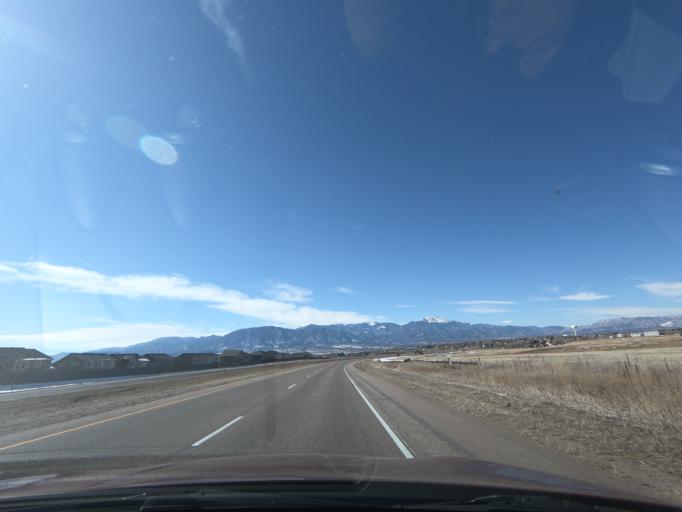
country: US
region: Colorado
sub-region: El Paso County
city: Security-Widefield
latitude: 38.7661
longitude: -104.7132
